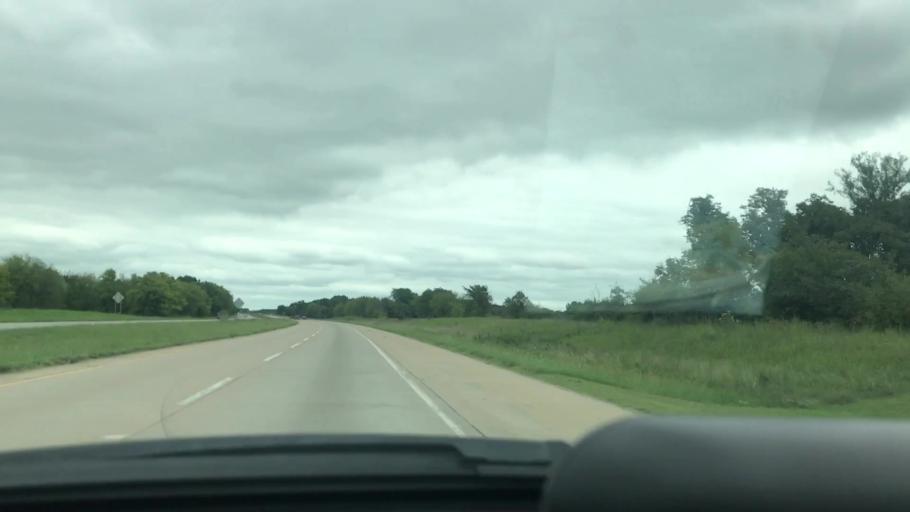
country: US
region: Oklahoma
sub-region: Mayes County
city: Chouteau
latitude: 36.1989
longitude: -95.3410
